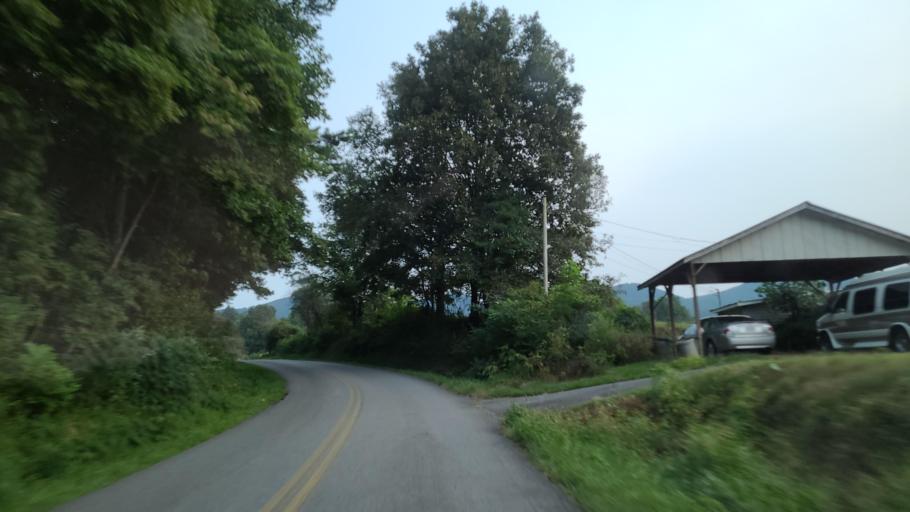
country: US
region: Georgia
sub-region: Union County
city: Blairsville
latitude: 34.8338
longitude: -84.0594
